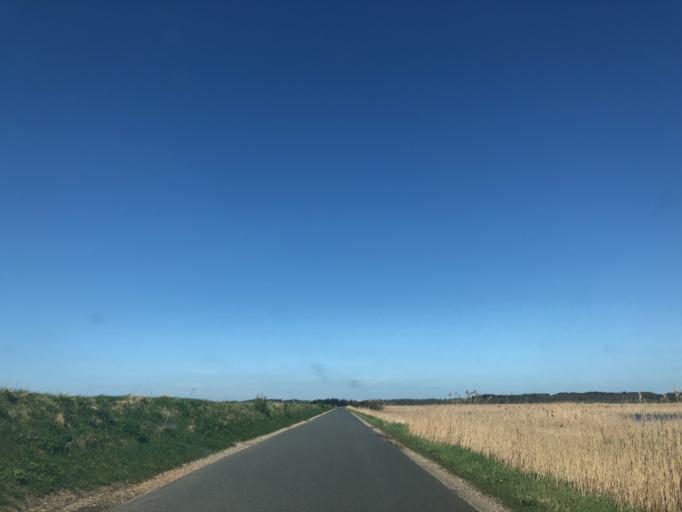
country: DK
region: Central Jutland
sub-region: Holstebro Kommune
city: Vinderup
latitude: 56.5473
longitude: 8.7697
